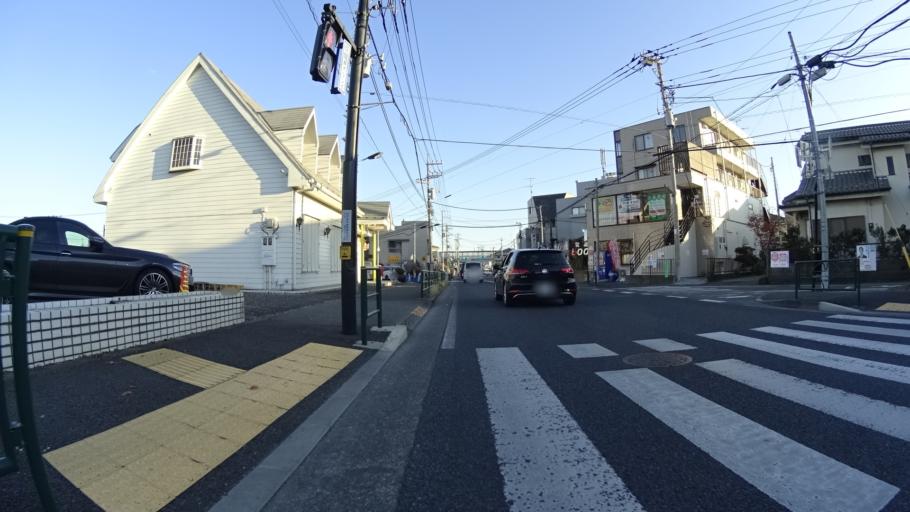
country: JP
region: Tokyo
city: Hachioji
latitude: 35.6692
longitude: 139.3006
